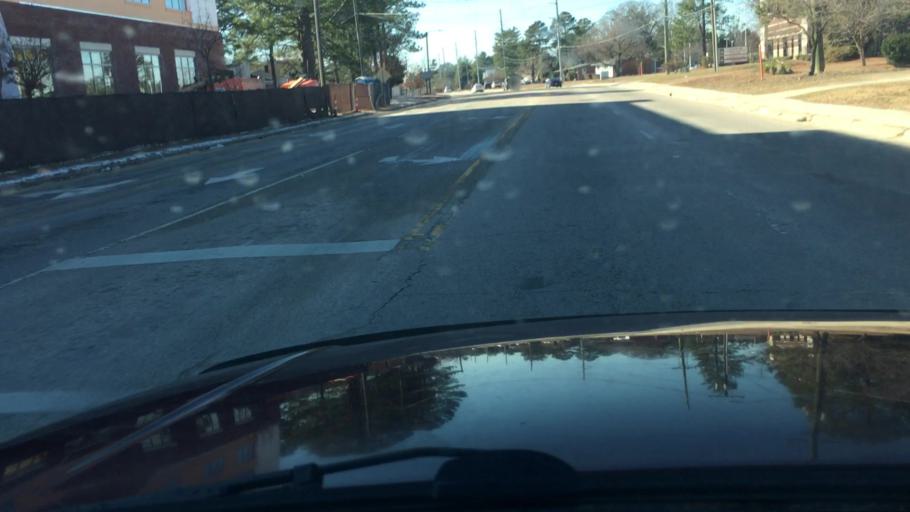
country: US
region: North Carolina
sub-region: Cumberland County
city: Fayetteville
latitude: 35.0299
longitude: -78.9335
